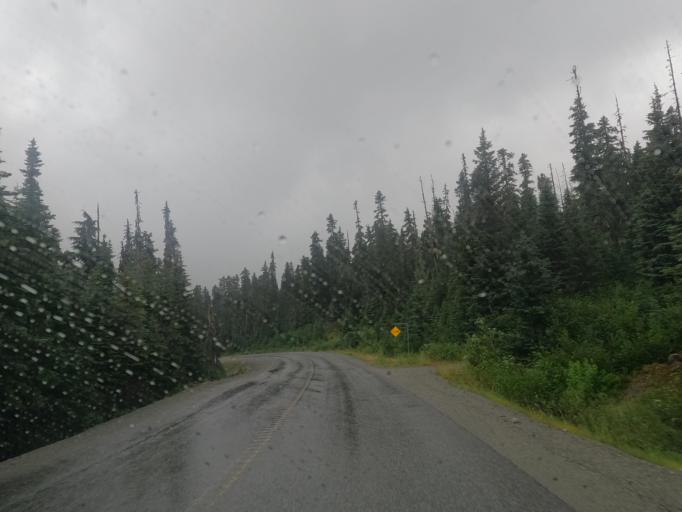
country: CA
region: British Columbia
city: Pemberton
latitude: 50.3866
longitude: -122.4662
